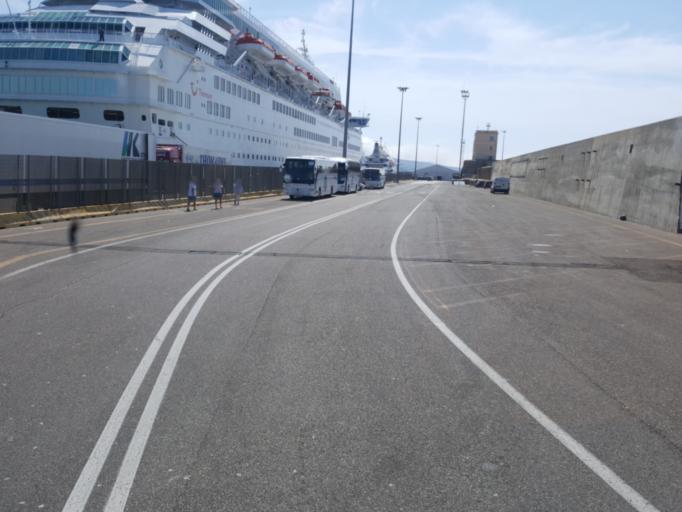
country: IT
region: Latium
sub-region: Citta metropolitana di Roma Capitale
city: Civitavecchia
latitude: 42.0925
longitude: 11.7828
